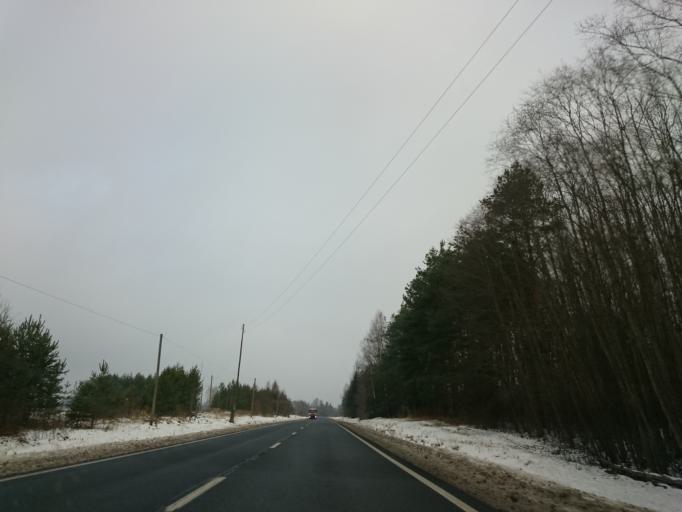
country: LV
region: Pargaujas
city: Stalbe
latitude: 57.3212
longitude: 24.9226
